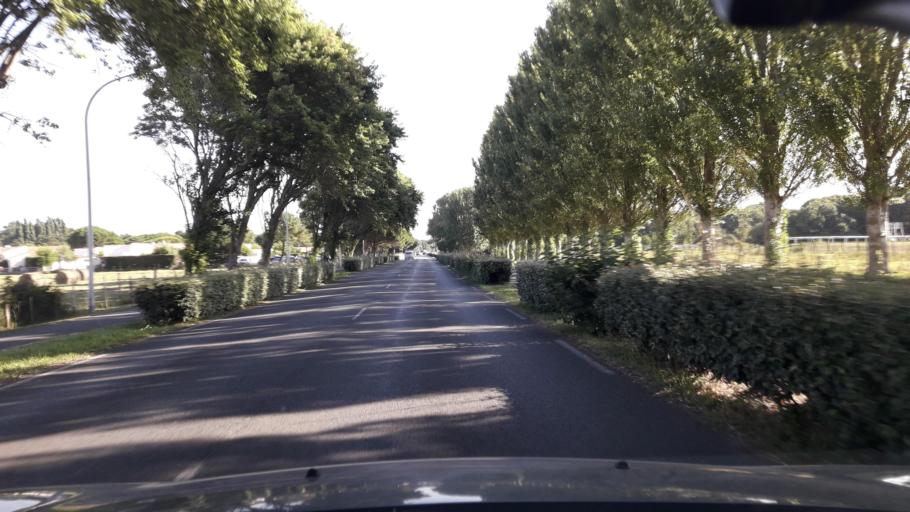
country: FR
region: Poitou-Charentes
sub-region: Departement de la Charente-Maritime
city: Les Mathes
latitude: 45.6977
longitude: -1.1737
